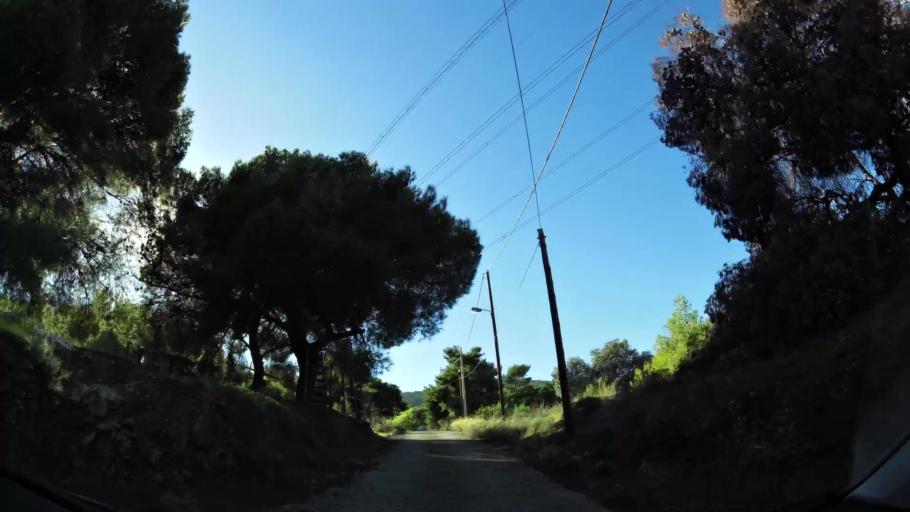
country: GR
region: Attica
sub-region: Nomarchia Anatolikis Attikis
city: Leondarion
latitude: 37.9872
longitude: 23.8422
